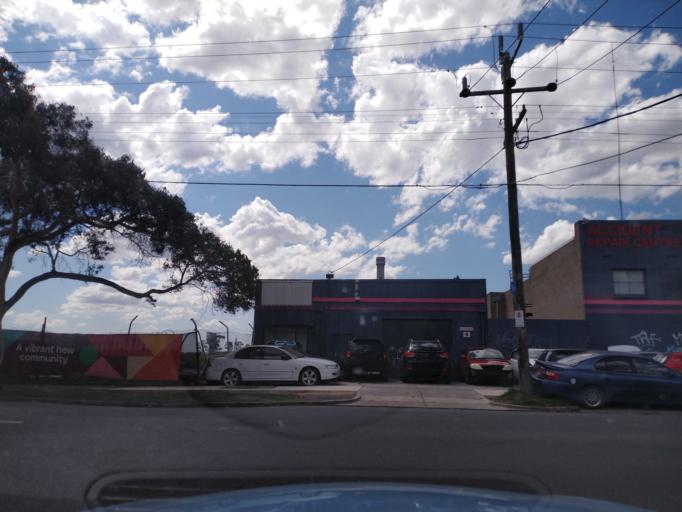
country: AU
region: Victoria
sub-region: Hobsons Bay
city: South Kingsville
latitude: -37.8331
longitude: 144.8657
